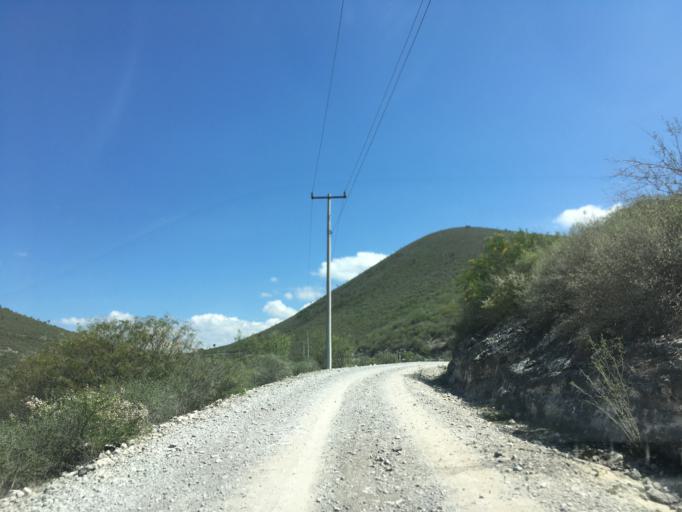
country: MX
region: Hidalgo
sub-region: Metztitlan
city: Fontezuelas
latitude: 20.6370
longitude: -98.8467
